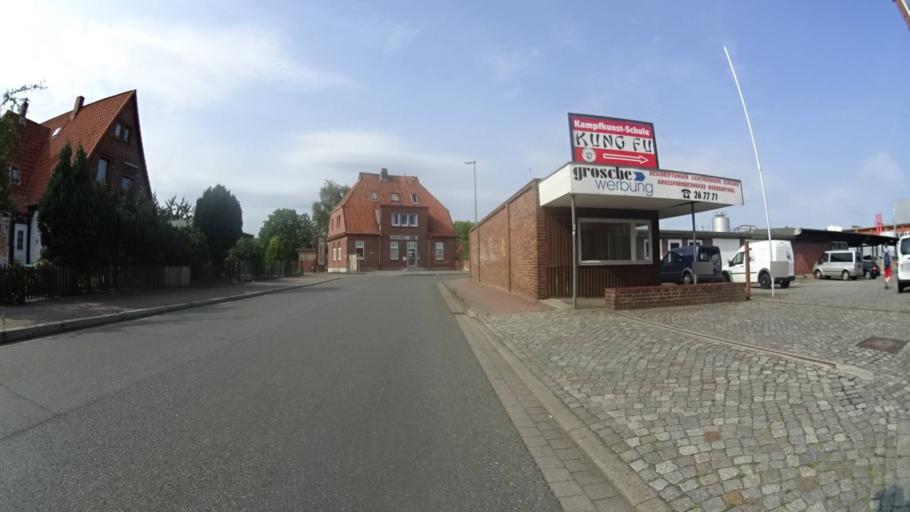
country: DE
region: Lower Saxony
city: Lueneburg
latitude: 53.2649
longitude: 10.4181
